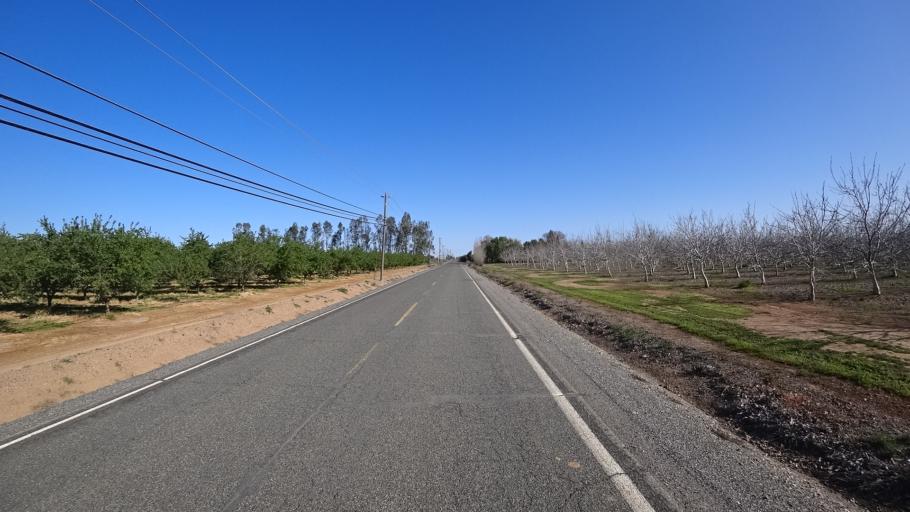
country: US
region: California
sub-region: Glenn County
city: Orland
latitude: 39.7842
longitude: -122.1041
